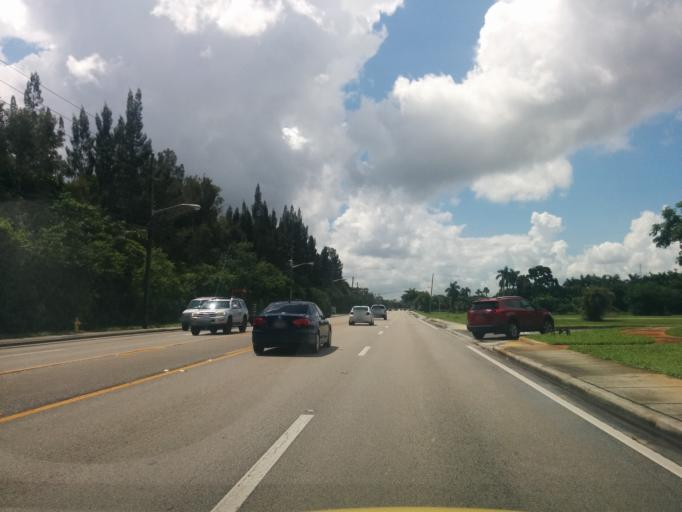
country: US
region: Florida
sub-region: Broward County
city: Davie
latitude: 26.0504
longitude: -80.2317
